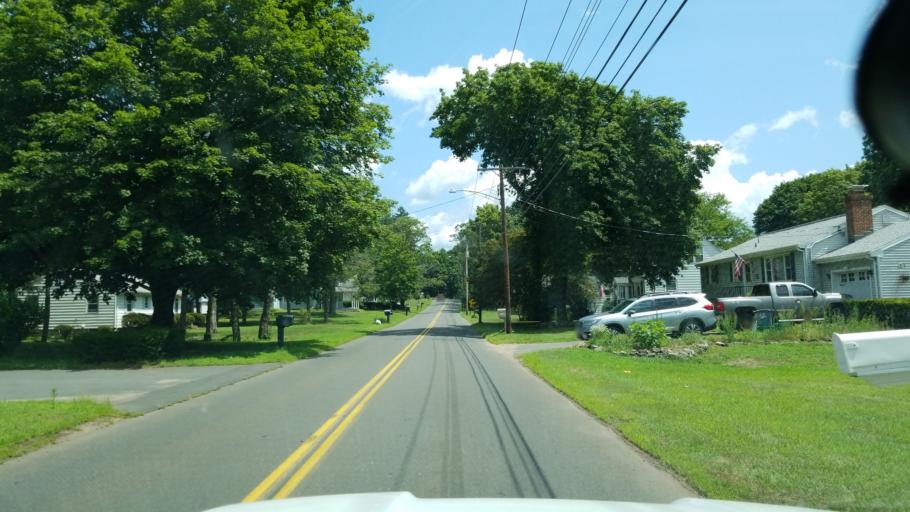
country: US
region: Connecticut
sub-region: New Haven County
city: North Haven
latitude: 41.3513
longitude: -72.8598
